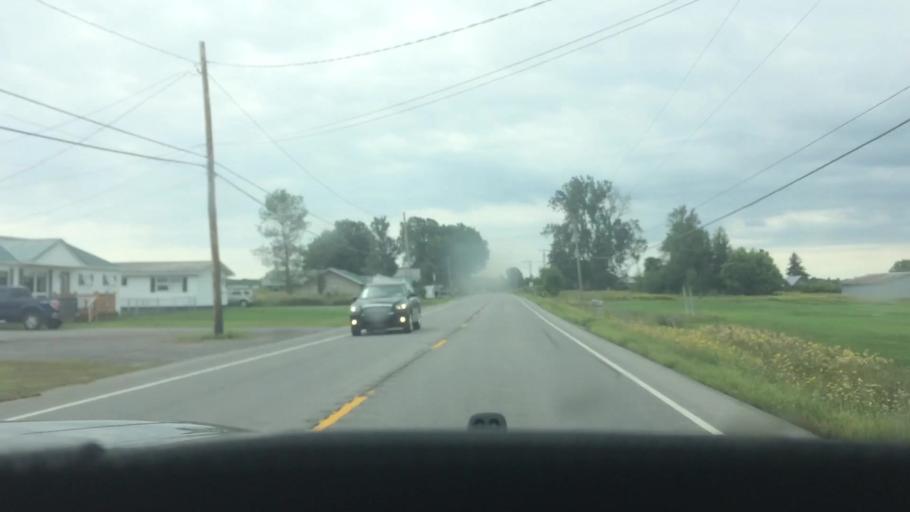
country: US
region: New York
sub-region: St. Lawrence County
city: Ogdensburg
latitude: 44.6694
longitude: -75.4707
